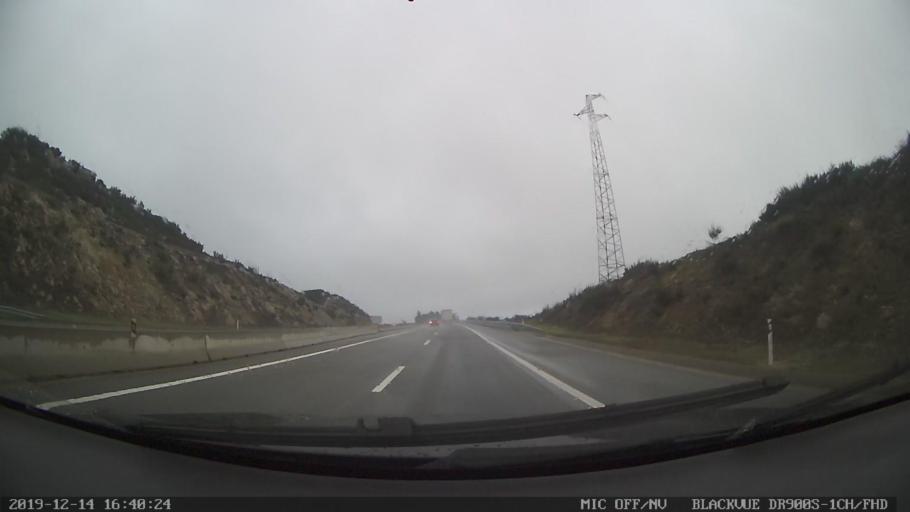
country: PT
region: Vila Real
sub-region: Murca
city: Murca
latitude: 41.3778
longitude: -7.5222
